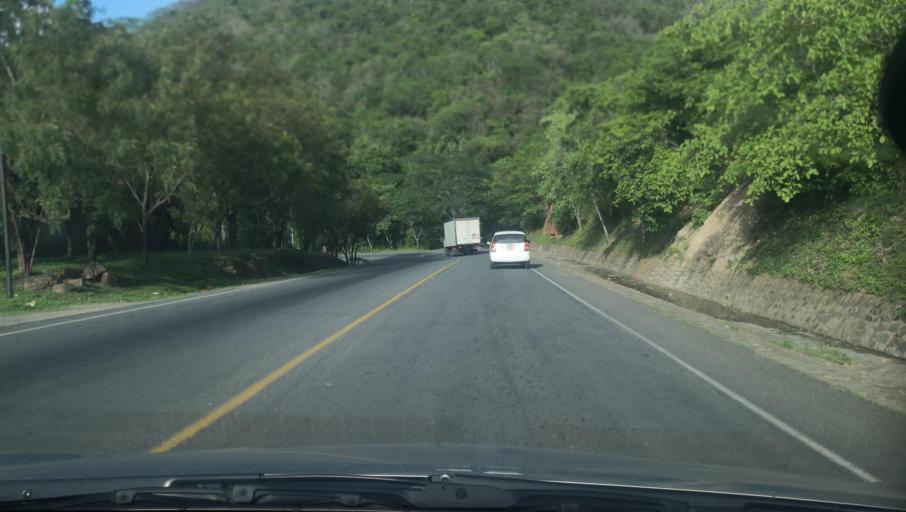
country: NI
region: Madriz
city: Totogalpa
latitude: 13.5883
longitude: -86.4725
